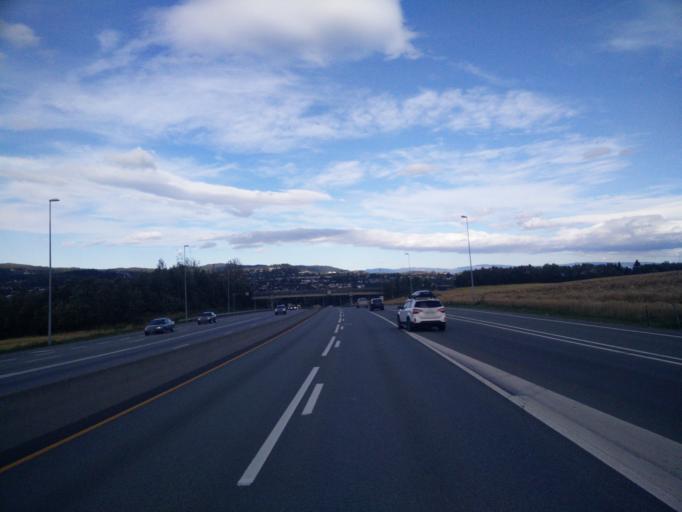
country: NO
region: Sor-Trondelag
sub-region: Trondheim
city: Trondheim
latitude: 63.3730
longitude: 10.3789
